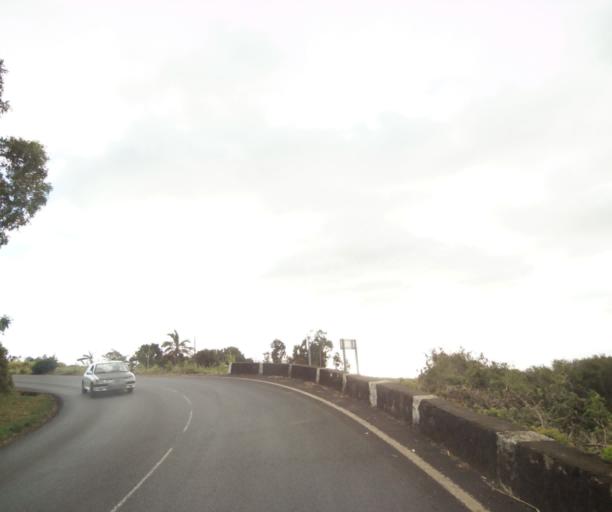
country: RE
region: Reunion
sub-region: Reunion
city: Trois-Bassins
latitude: -21.0649
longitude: 55.2793
